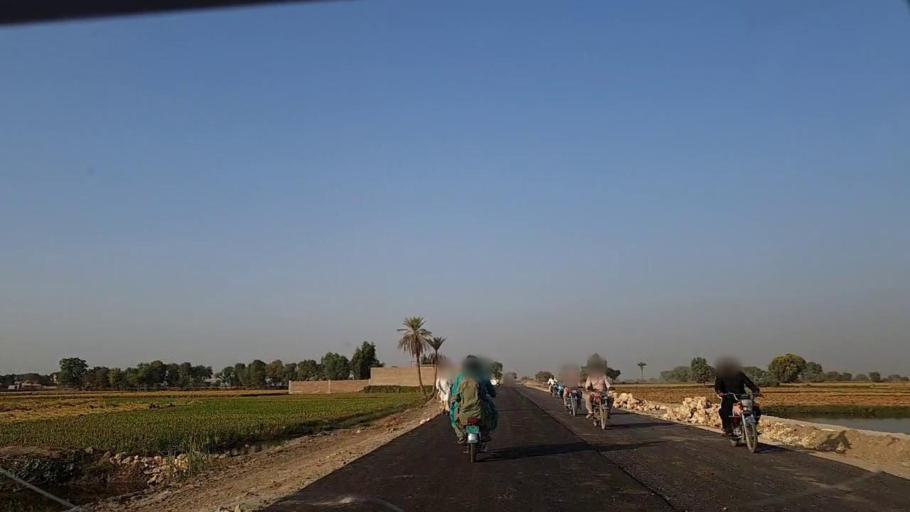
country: PK
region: Sindh
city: Rustam jo Goth
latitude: 27.9705
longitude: 68.8033
